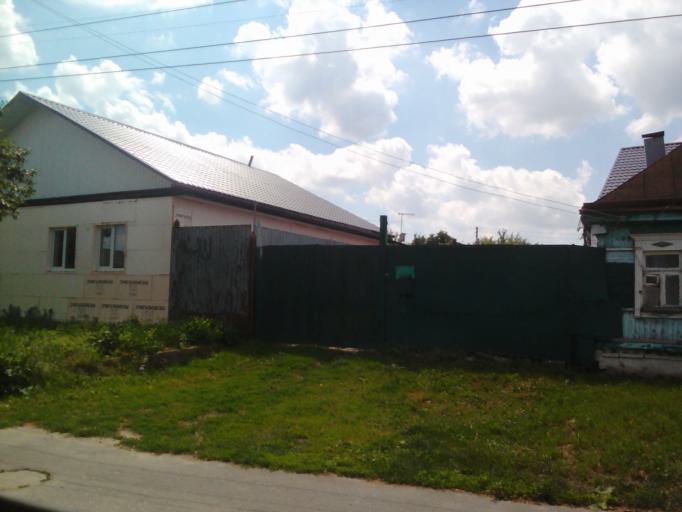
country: RU
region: Kursk
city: Kursk
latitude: 51.7405
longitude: 36.1723
